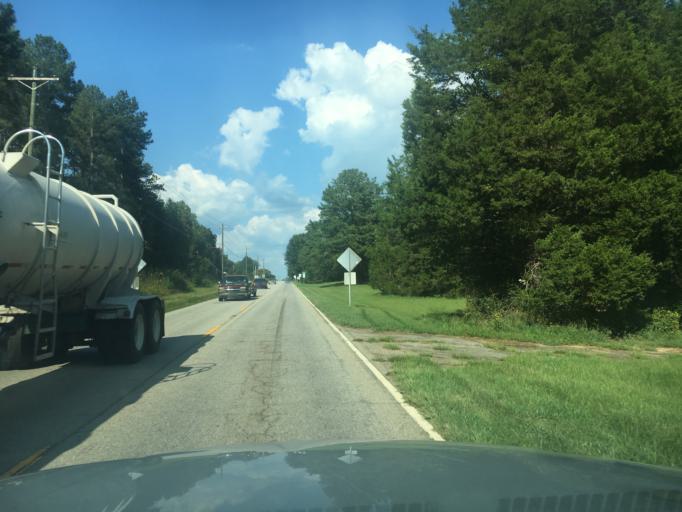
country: US
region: South Carolina
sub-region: Pickens County
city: Liberty
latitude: 34.7275
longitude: -82.6743
